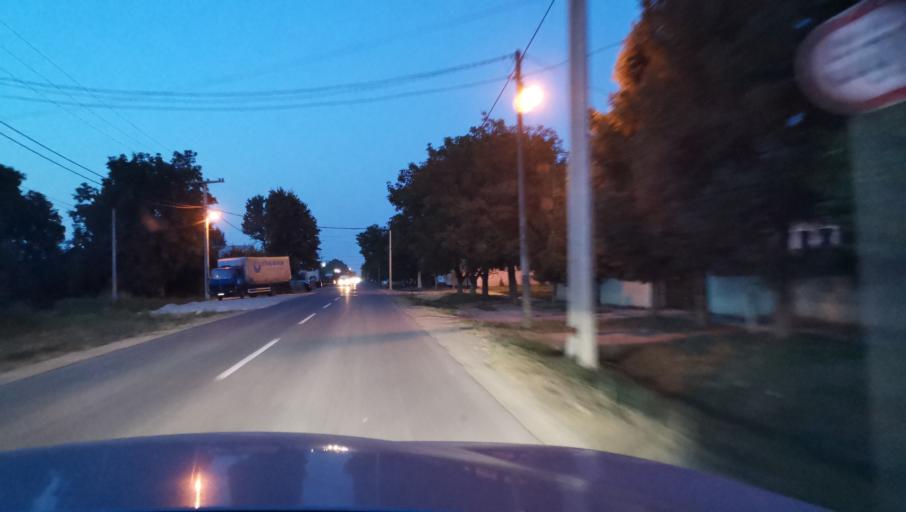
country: RS
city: Boljevci
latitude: 44.7245
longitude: 20.2384
